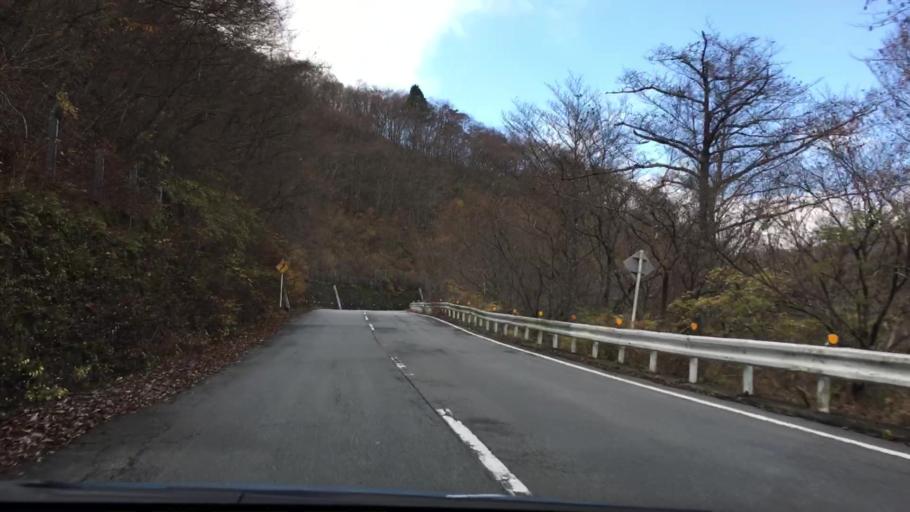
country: JP
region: Shizuoka
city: Gotemba
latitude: 35.4040
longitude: 138.9182
